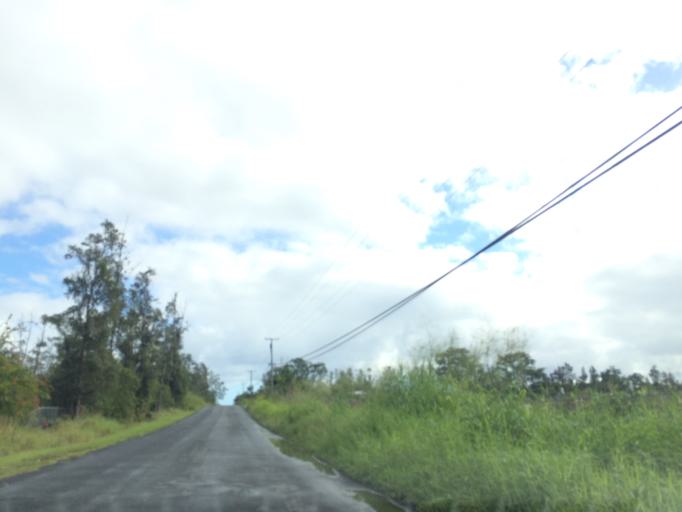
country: US
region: Hawaii
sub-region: Hawaii County
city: Orchidlands Estates
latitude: 19.5554
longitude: -154.9999
